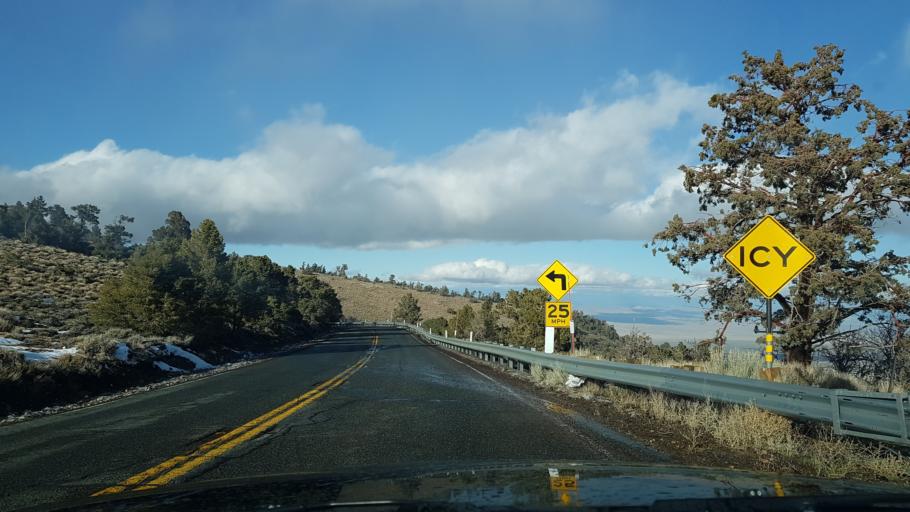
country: US
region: California
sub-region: San Bernardino County
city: Big Bear City
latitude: 34.2910
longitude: -116.8025
